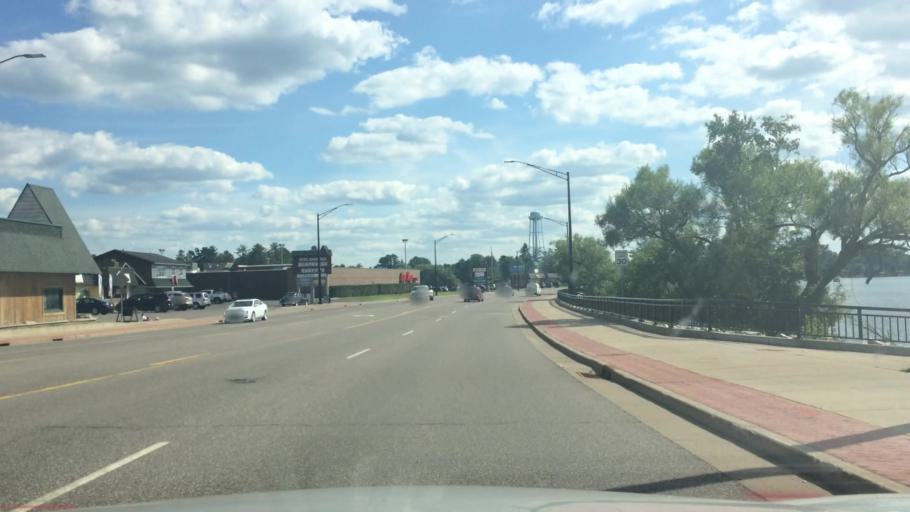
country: US
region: Wisconsin
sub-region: Vilas County
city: Lac du Flambeau
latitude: 45.8783
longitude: -89.7037
